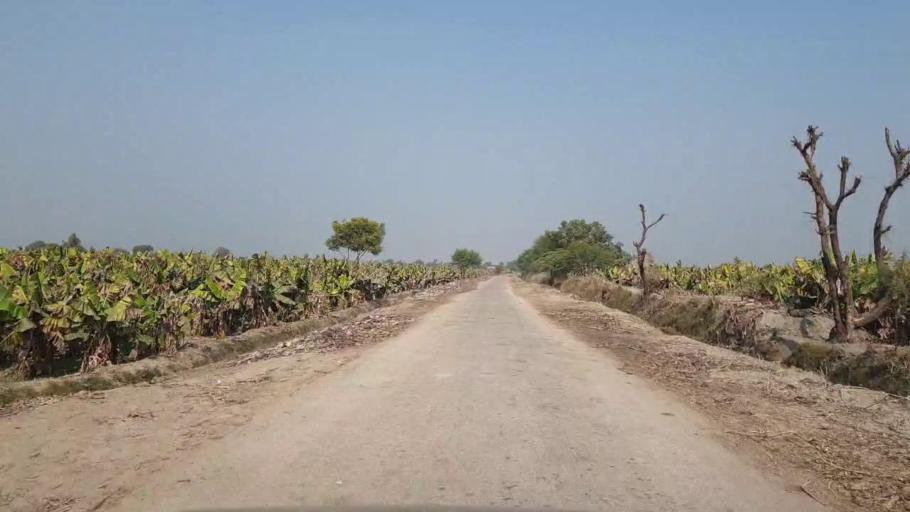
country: PK
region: Sindh
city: Bhit Shah
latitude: 25.7831
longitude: 68.4934
